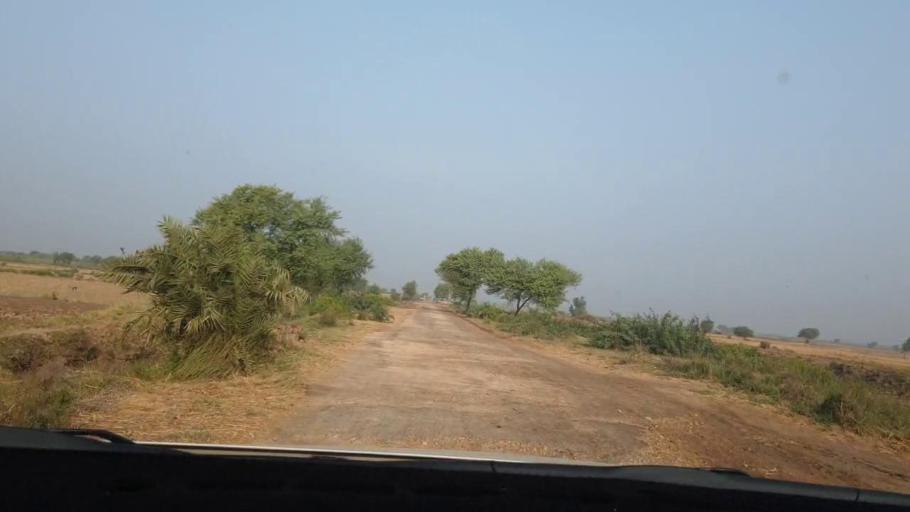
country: PK
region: Sindh
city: Tando Muhammad Khan
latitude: 25.0851
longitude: 68.4852
